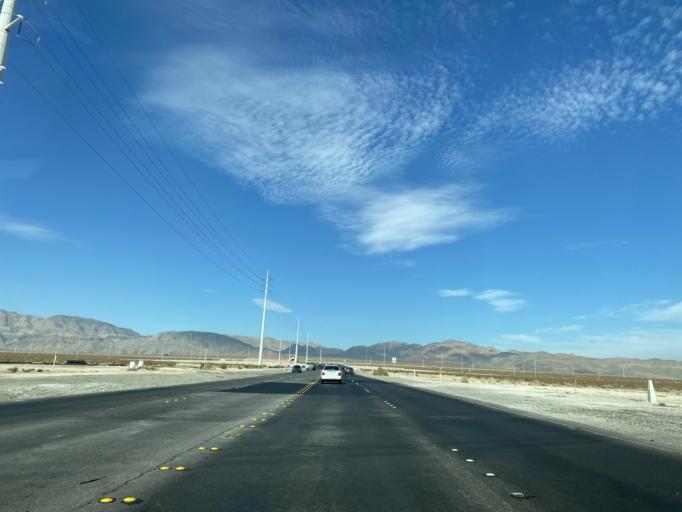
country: US
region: Nevada
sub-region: Clark County
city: Nellis Air Force Base
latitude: 36.2830
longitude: -115.0799
